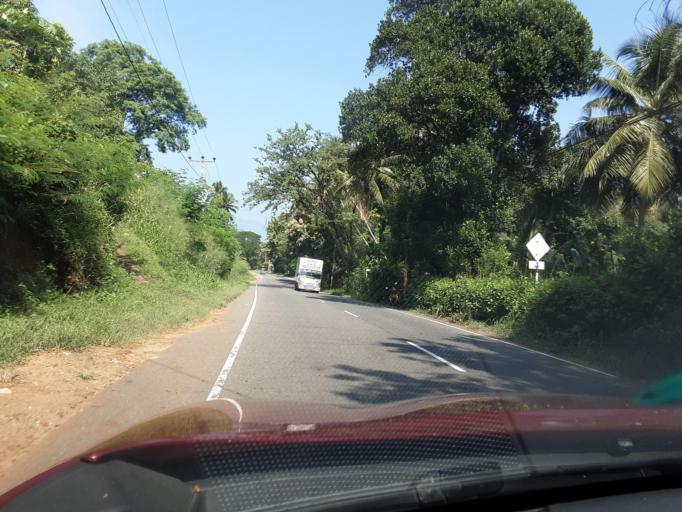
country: LK
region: Uva
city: Badulla
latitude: 7.1919
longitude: 81.0284
